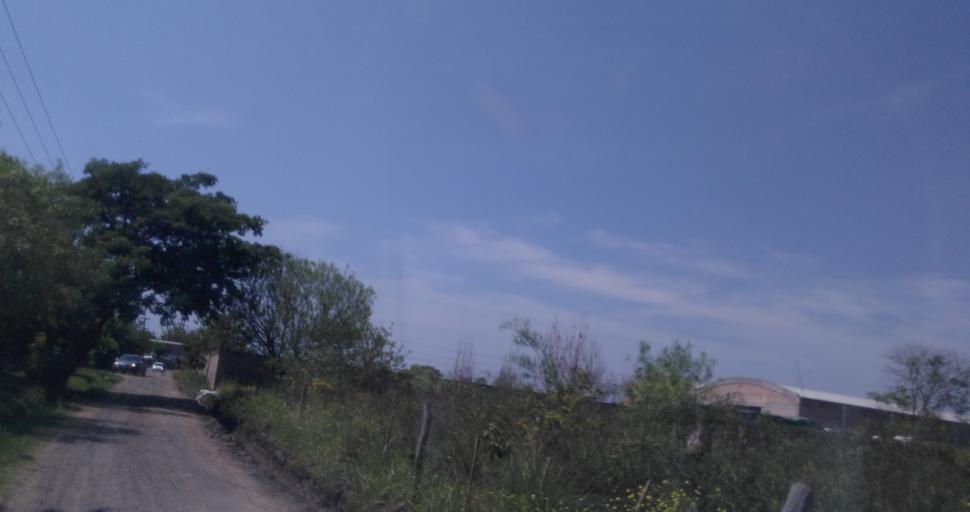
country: AR
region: Chaco
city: Fontana
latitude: -27.4038
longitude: -59.0013
